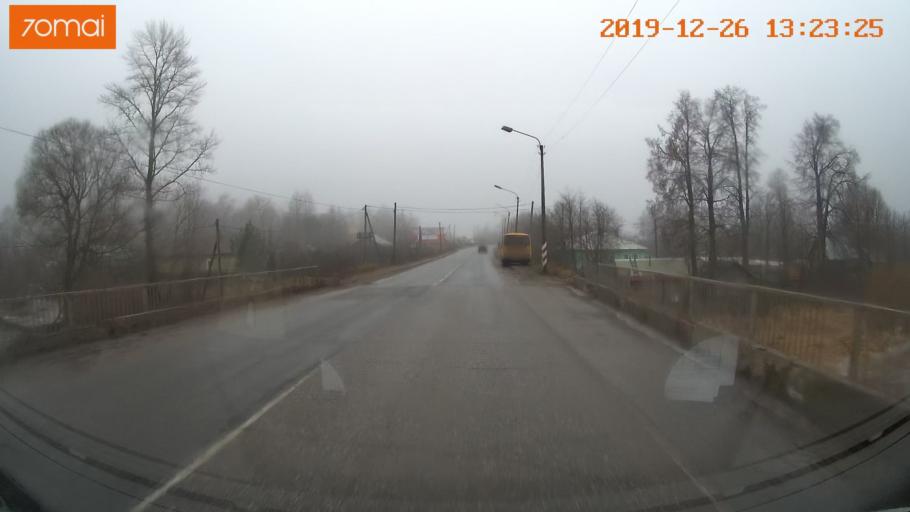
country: RU
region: Vologda
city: Cherepovets
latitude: 58.8911
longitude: 38.1843
